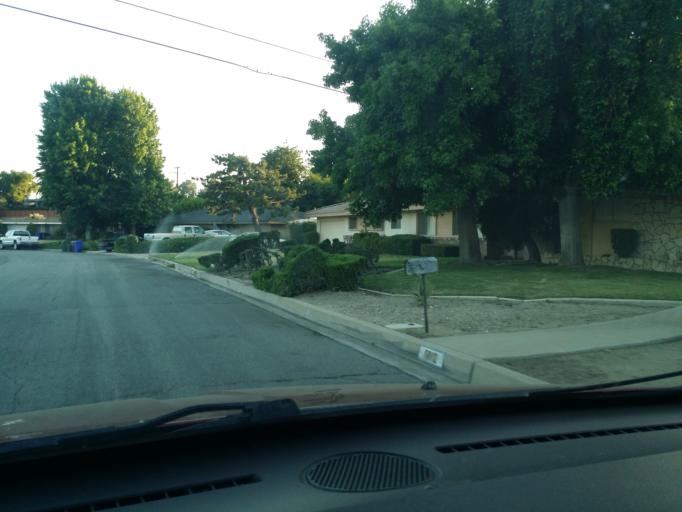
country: US
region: California
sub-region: San Bernardino County
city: Muscoy
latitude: 34.1480
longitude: -117.3790
